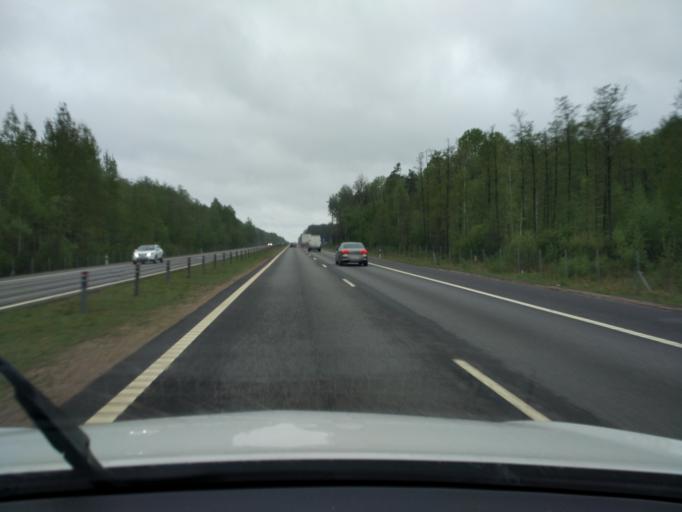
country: BY
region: Mogilev
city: Asipovichy
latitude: 53.2926
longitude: 28.8094
